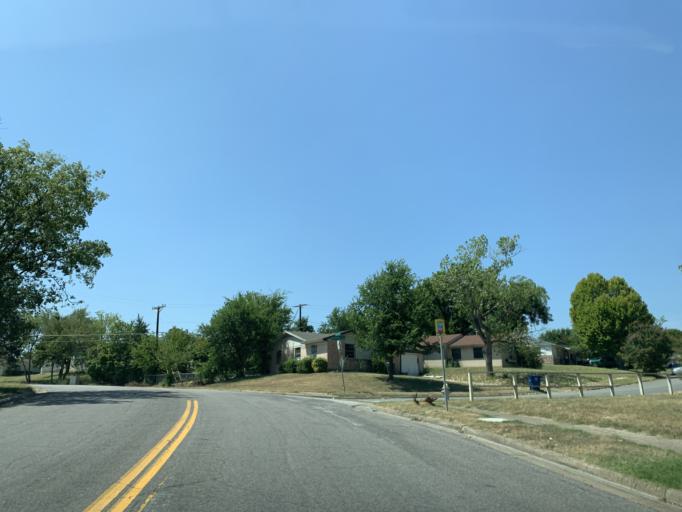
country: US
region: Texas
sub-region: Dallas County
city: Hutchins
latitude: 32.6757
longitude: -96.7484
